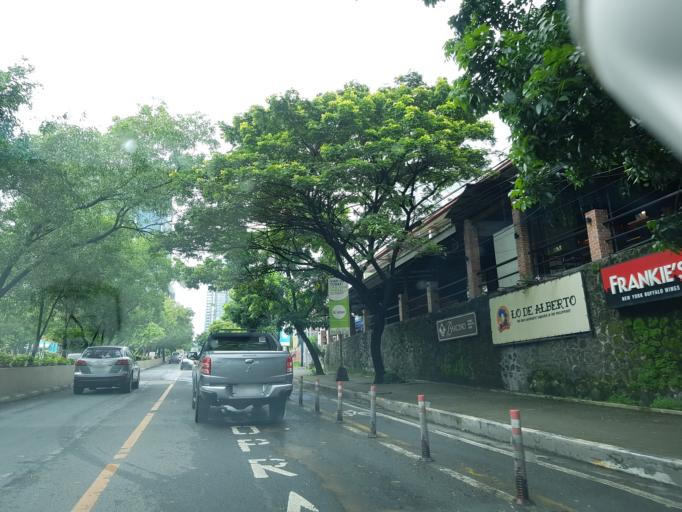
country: PH
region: Metro Manila
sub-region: Pasig
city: Pasig City
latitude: 14.5844
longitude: 121.0676
